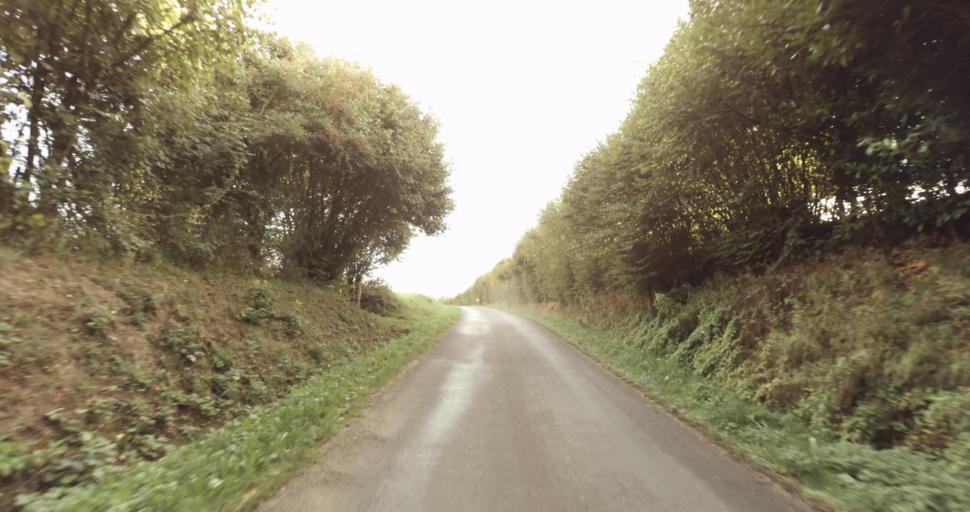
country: FR
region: Lower Normandy
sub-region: Departement de l'Orne
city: Sees
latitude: 48.6931
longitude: 0.2298
